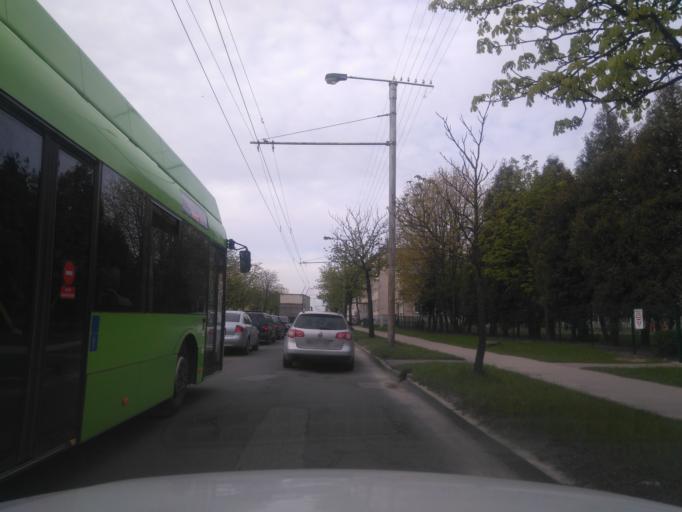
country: LT
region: Kauno apskritis
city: Dainava (Kaunas)
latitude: 54.9038
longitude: 23.9738
